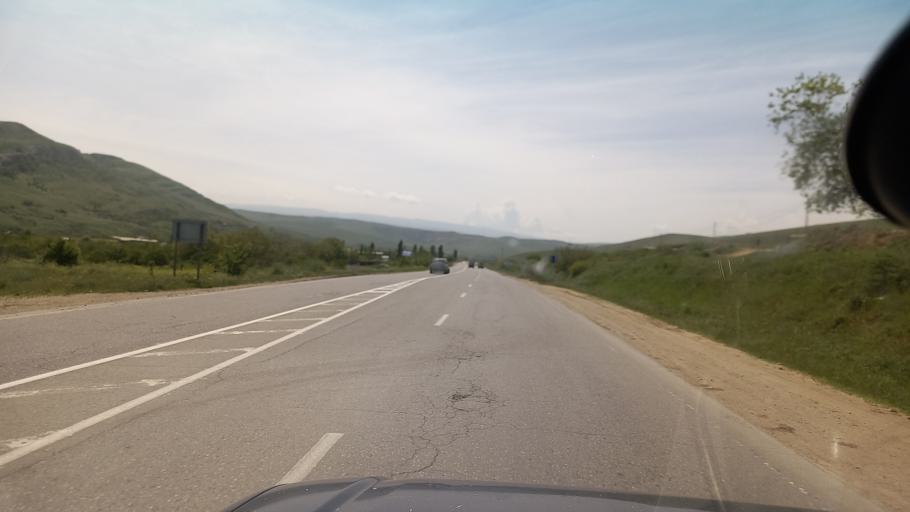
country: RU
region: Dagestan
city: Manas
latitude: 42.7092
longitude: 47.6377
